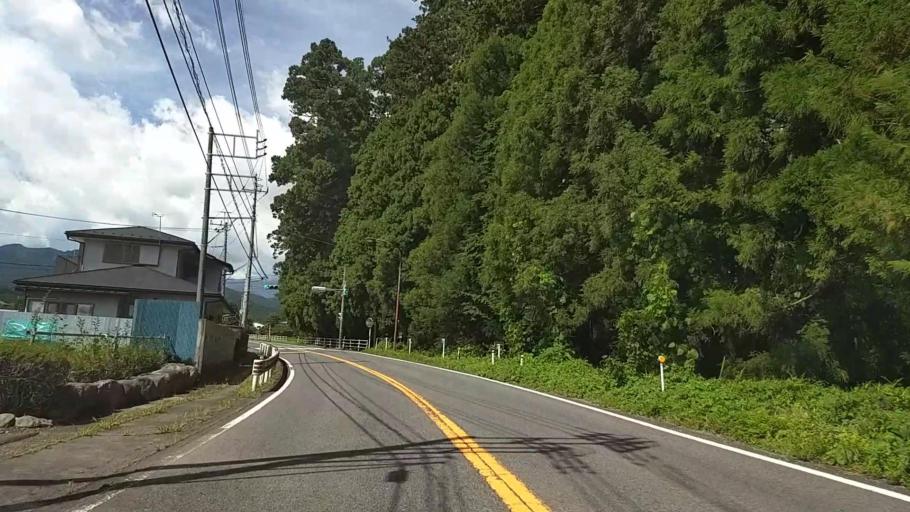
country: JP
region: Tochigi
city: Imaichi
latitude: 36.7325
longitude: 139.6614
